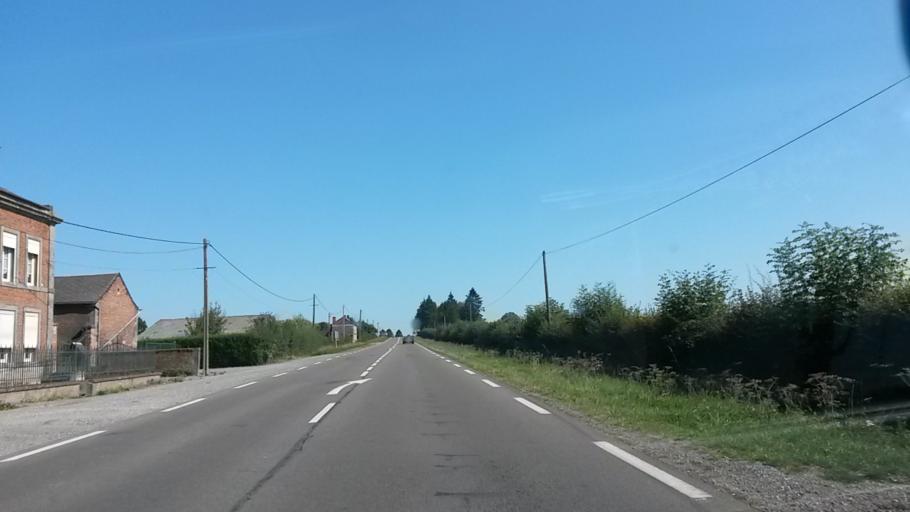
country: FR
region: Nord-Pas-de-Calais
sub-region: Departement du Nord
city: Avesnelles
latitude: 50.1496
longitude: 3.9514
